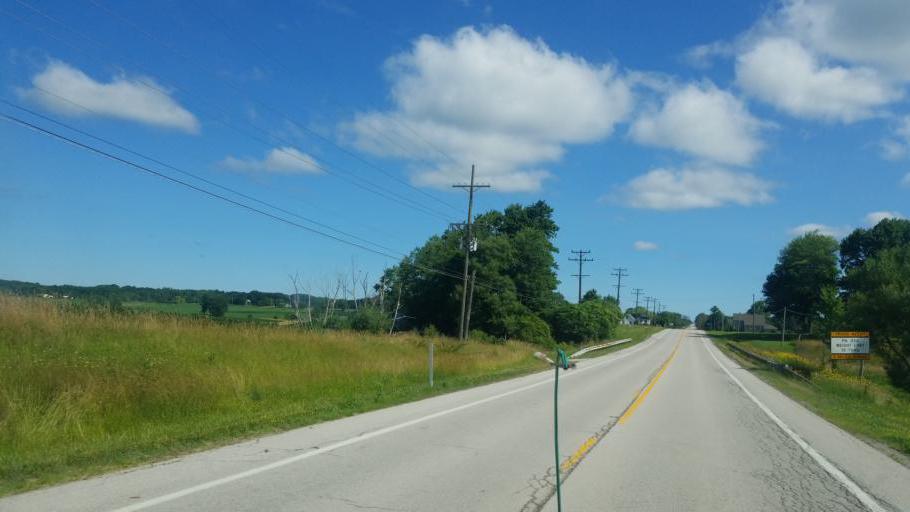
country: US
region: Ohio
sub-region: Ashtabula County
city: Conneaut
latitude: 41.8550
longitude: -80.5724
